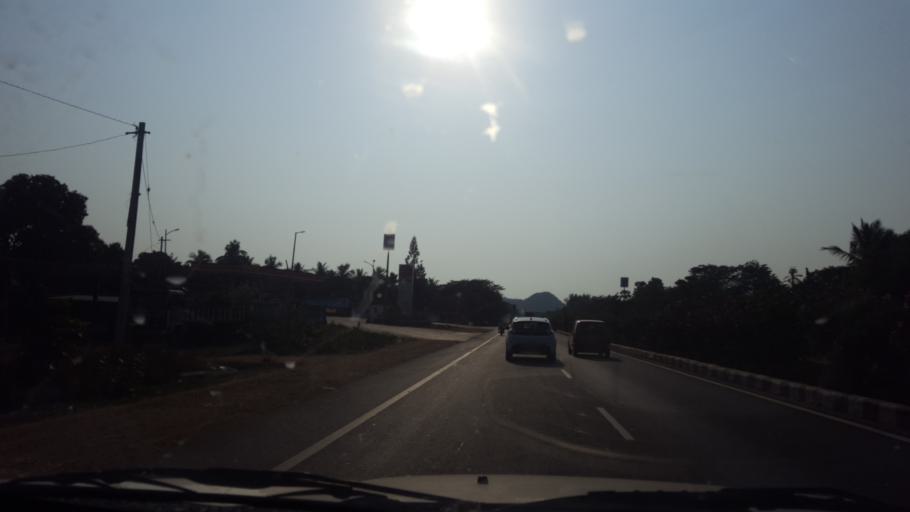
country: IN
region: Andhra Pradesh
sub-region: East Godavari
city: Tuni
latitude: 17.3944
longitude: 82.6651
